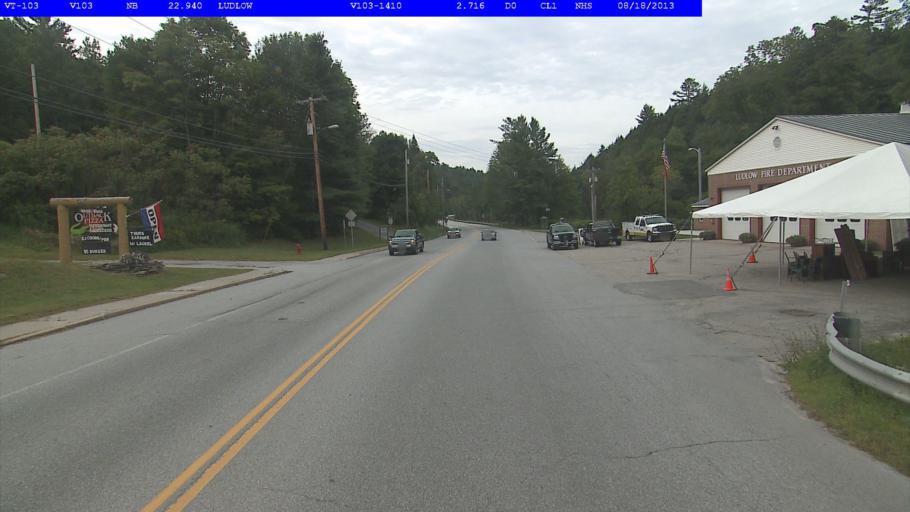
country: US
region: Vermont
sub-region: Windsor County
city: Chester
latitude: 43.4014
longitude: -72.7070
